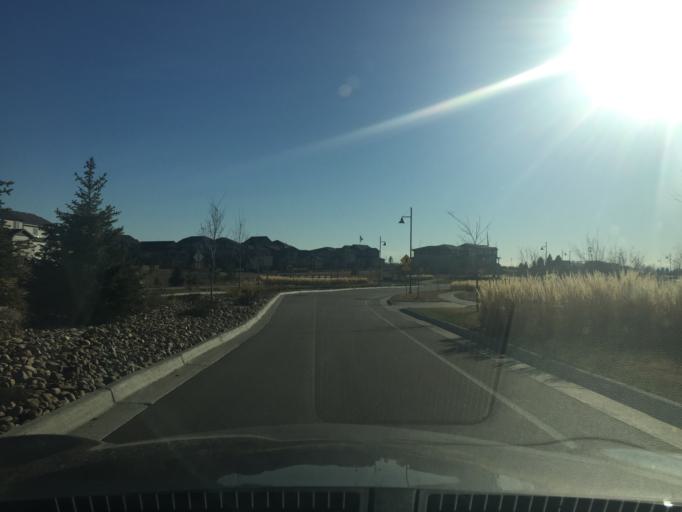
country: US
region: Colorado
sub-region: Boulder County
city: Erie
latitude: 40.0468
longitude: -105.0354
